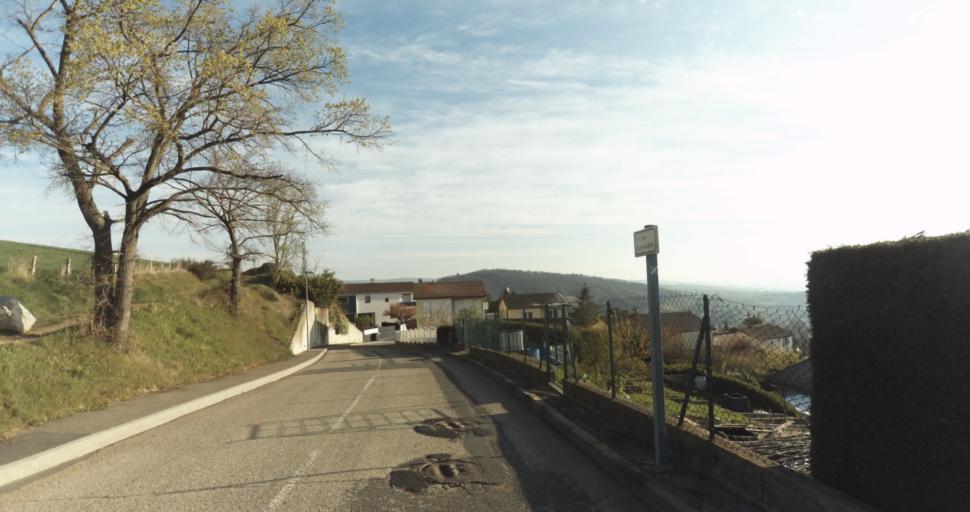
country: FR
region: Rhone-Alpes
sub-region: Departement de la Loire
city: Saint-Jean-Bonnefonds
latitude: 45.4517
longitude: 4.4413
